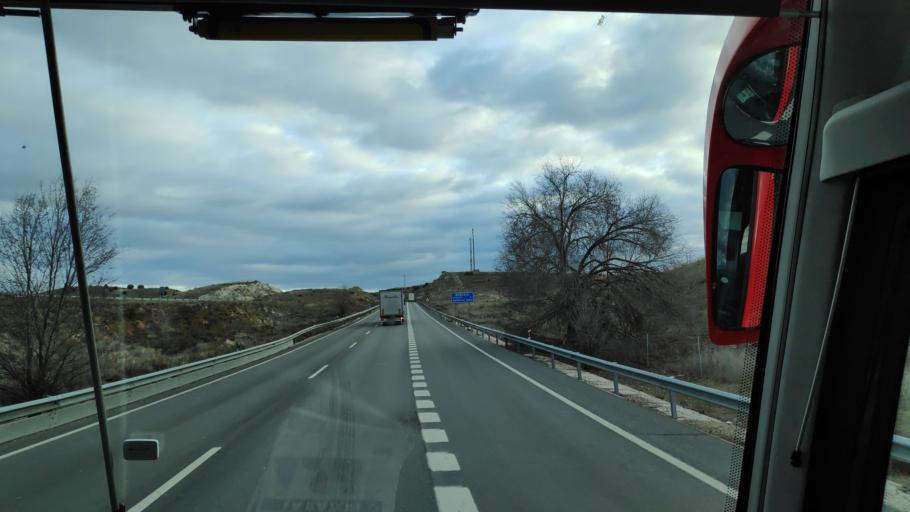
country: ES
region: Madrid
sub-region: Provincia de Madrid
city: Tielmes
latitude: 40.2055
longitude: -3.3149
